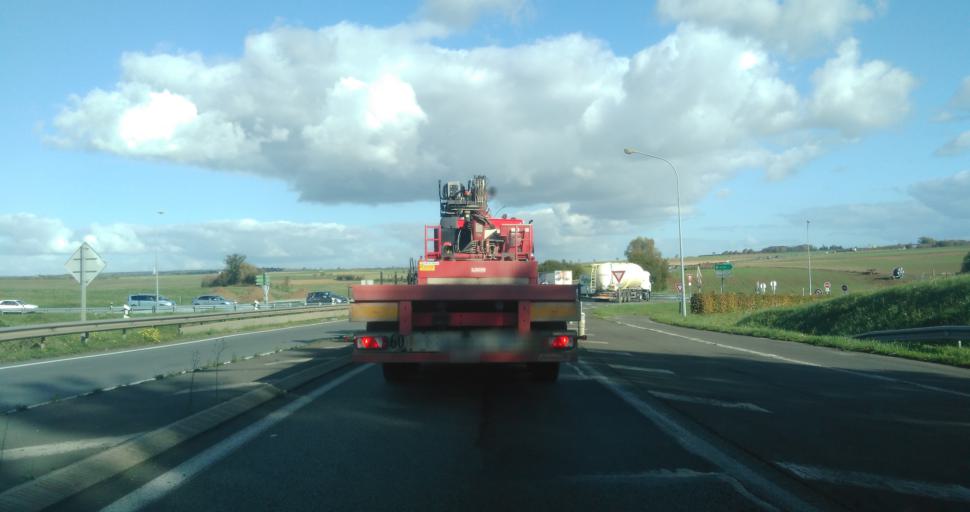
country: FR
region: Nord-Pas-de-Calais
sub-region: Departement du Pas-de-Calais
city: Anzin-Saint-Aubin
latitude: 50.3216
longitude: 2.7304
